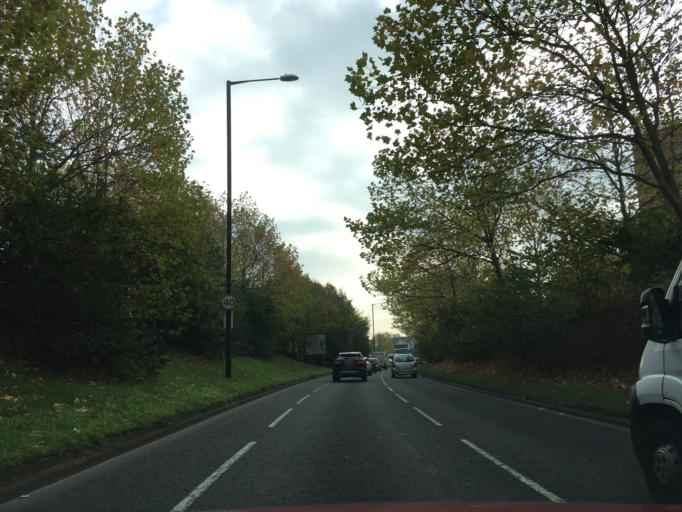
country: GB
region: England
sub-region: Bristol
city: Bristol
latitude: 51.4650
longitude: -2.5728
